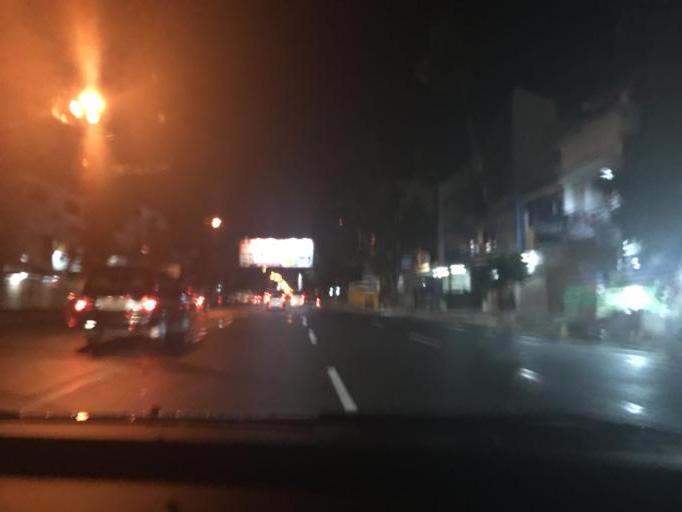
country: ID
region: West Java
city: Bandung
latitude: -6.9133
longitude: 107.6346
